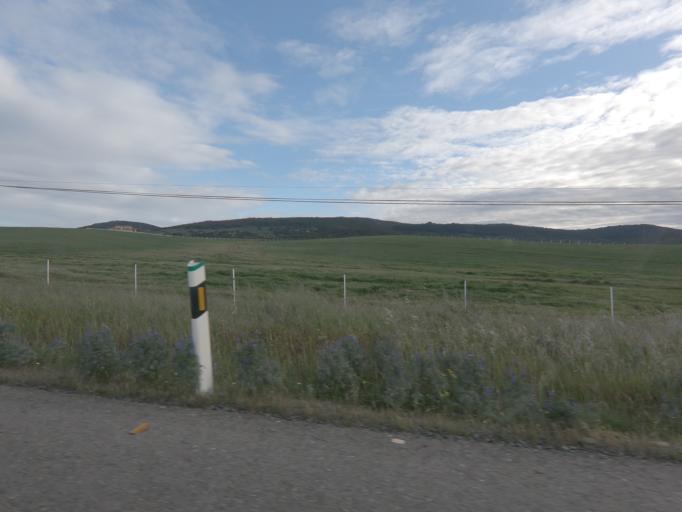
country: ES
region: Extremadura
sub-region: Provincia de Caceres
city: Pedroso de Acim
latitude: 39.8405
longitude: -6.3981
